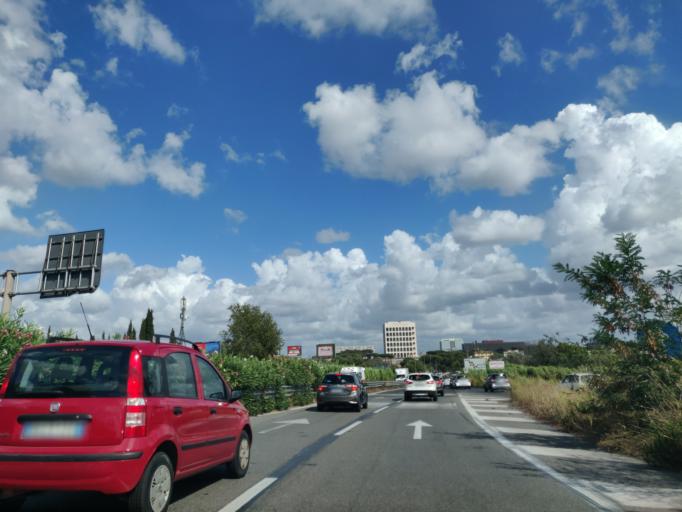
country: VA
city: Vatican City
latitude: 41.8405
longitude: 12.4552
